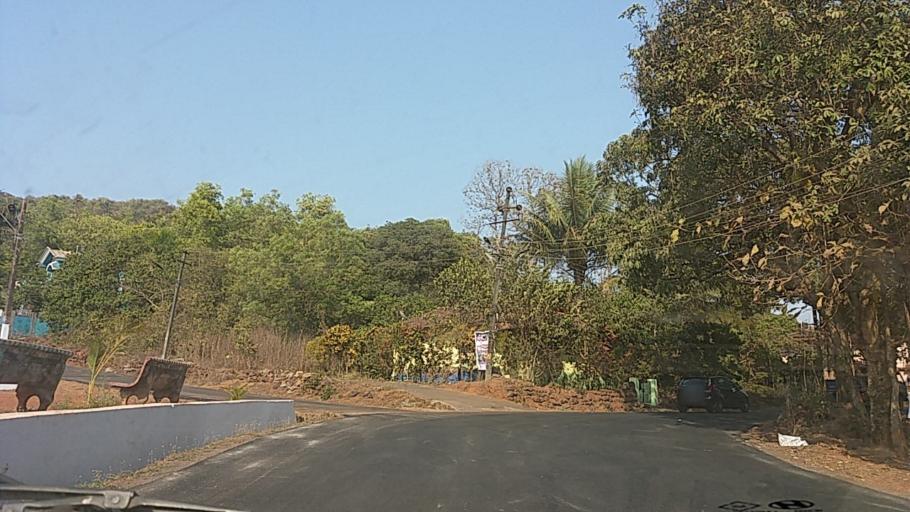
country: IN
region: Goa
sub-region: South Goa
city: Raia
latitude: 15.3080
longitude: 73.9667
